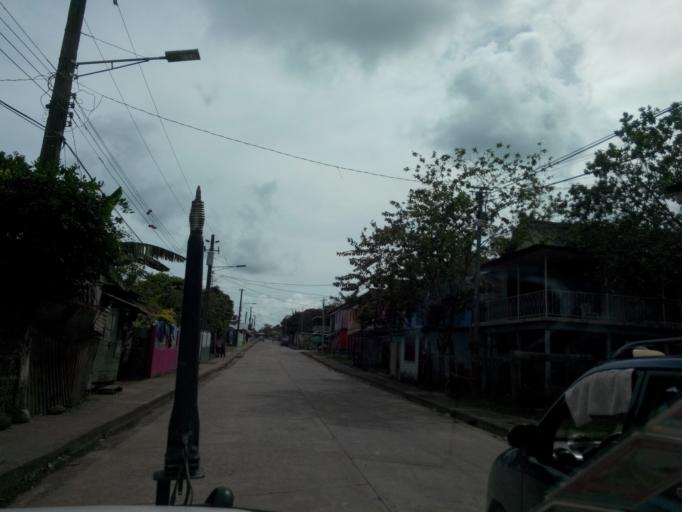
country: NI
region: Atlantico Sur
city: Bluefields
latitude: 12.0015
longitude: -83.7666
